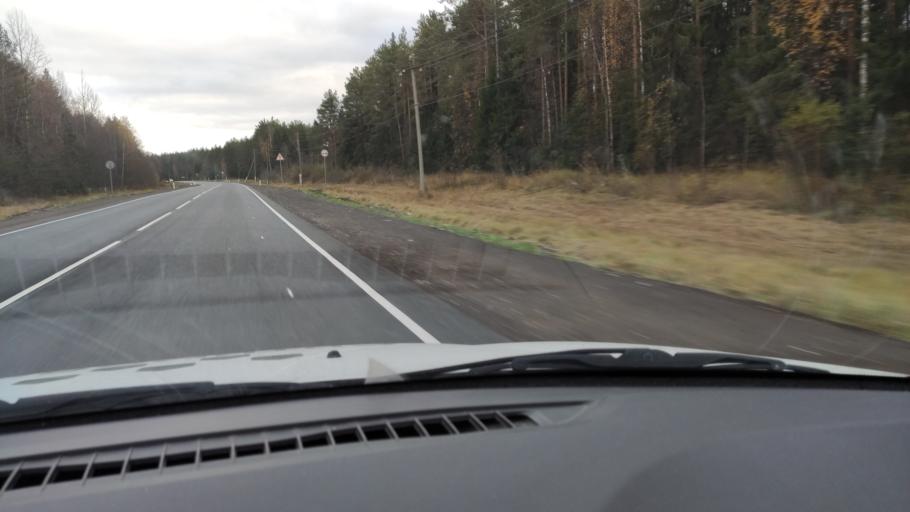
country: RU
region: Kirov
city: Belaya Kholunitsa
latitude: 58.8430
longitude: 50.7708
